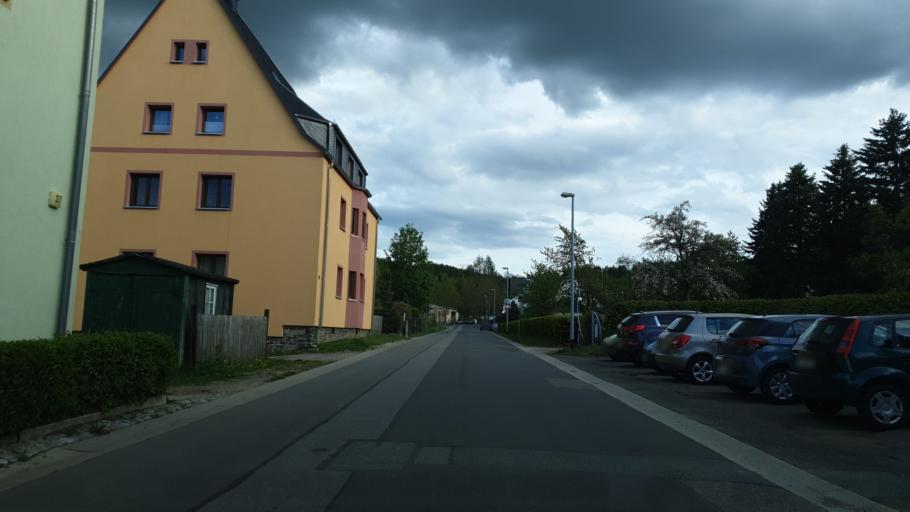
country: DE
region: Saxony
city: Hohndorf
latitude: 50.7273
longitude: 12.6666
